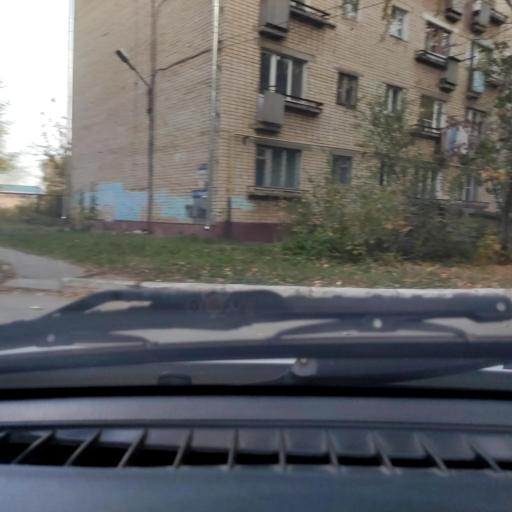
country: RU
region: Samara
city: Tol'yatti
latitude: 53.5132
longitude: 49.4396
